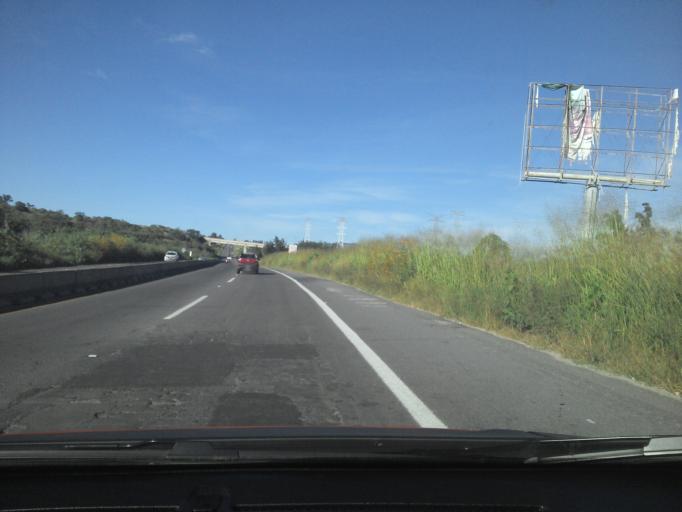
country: MX
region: Jalisco
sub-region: Tala
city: Los Ruisenores
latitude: 20.6831
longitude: -103.6948
